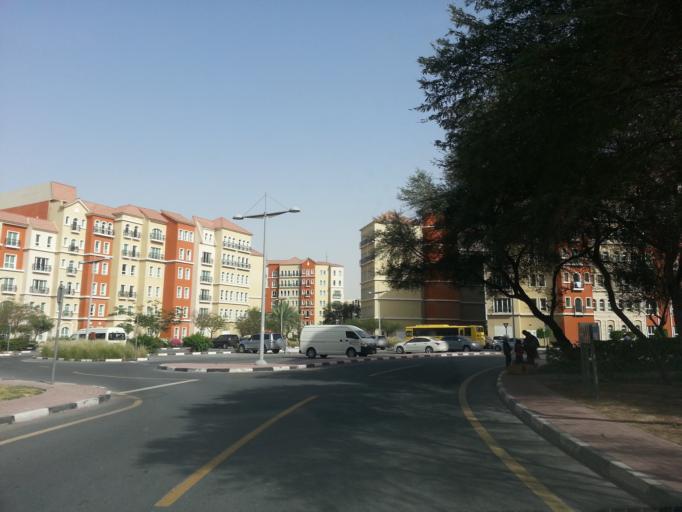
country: AE
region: Dubai
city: Dubai
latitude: 25.0371
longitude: 55.1497
